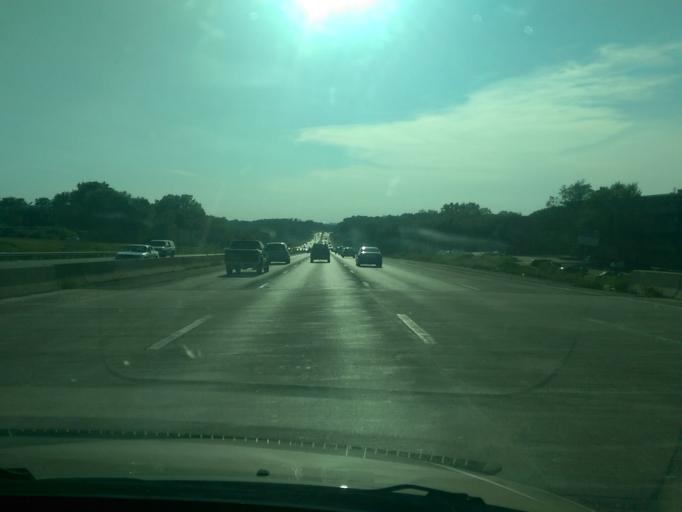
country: US
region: Missouri
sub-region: Jackson County
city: Raytown
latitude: 39.0474
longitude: -94.4477
